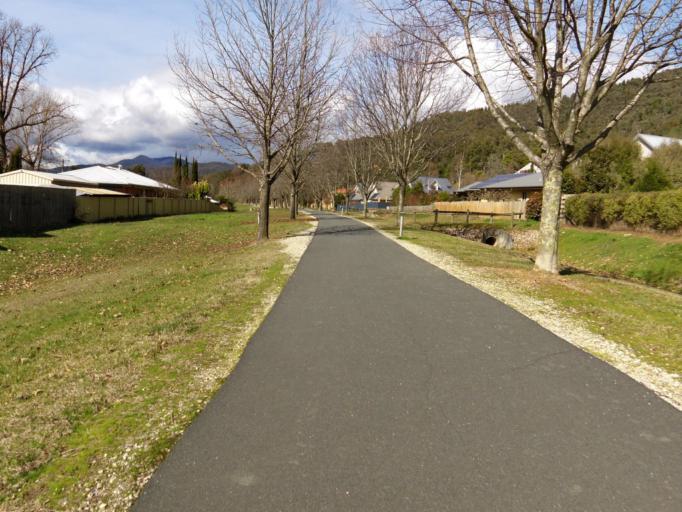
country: AU
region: Victoria
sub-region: Alpine
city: Mount Beauty
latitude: -36.7292
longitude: 146.9502
